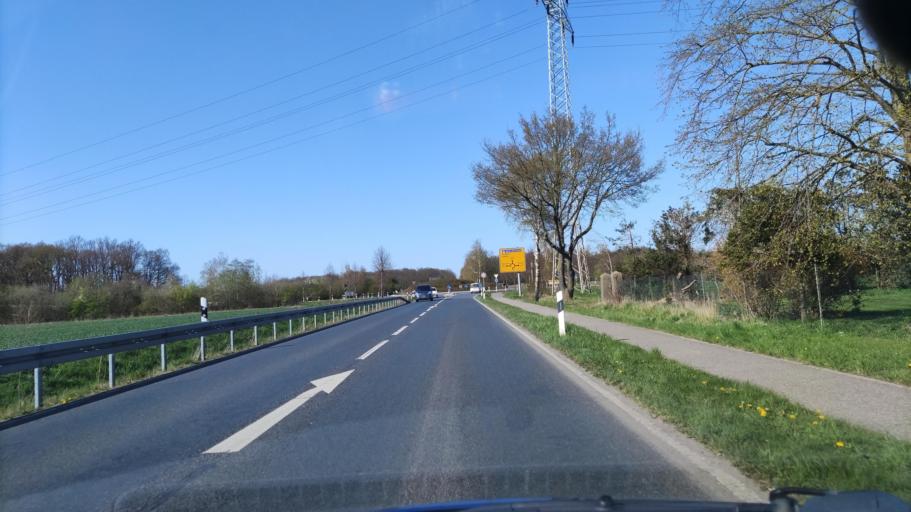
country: DE
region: Lower Saxony
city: Sehnde
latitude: 52.3301
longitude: 9.9688
